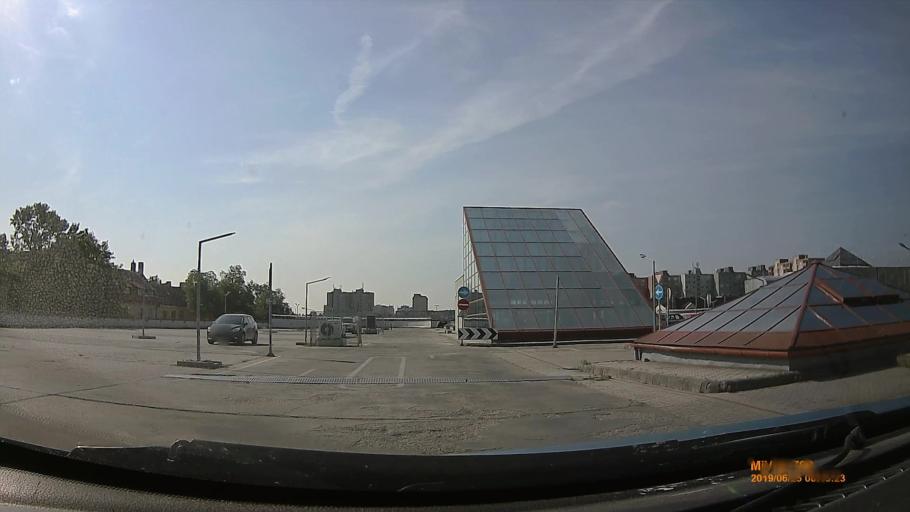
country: HU
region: Fejer
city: Szekesfehervar
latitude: 47.1907
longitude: 18.4066
